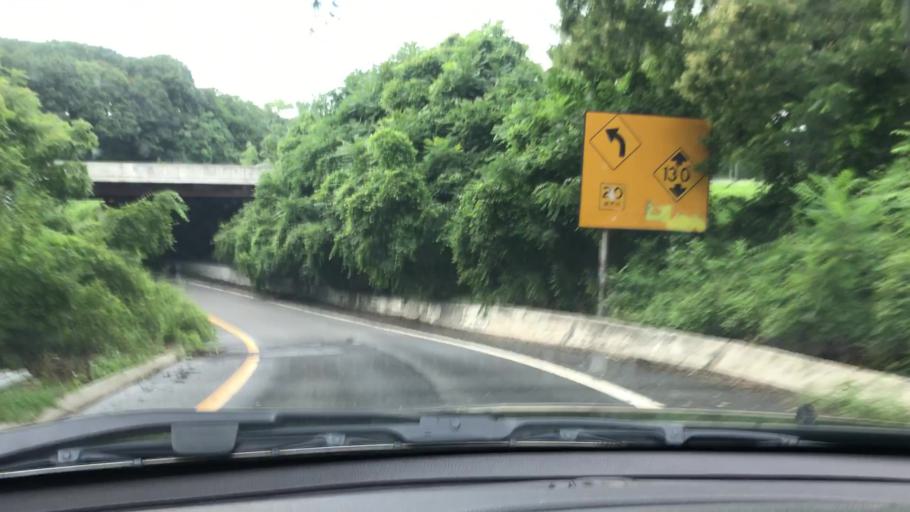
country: US
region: New York
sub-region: Westchester County
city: Tuckahoe
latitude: 40.9436
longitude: -73.8007
